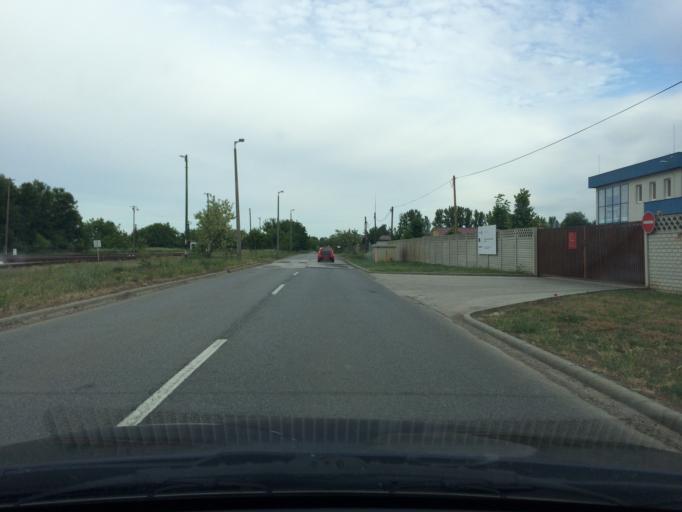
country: HU
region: Szabolcs-Szatmar-Bereg
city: Tiszavasvari
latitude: 47.9424
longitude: 21.3773
